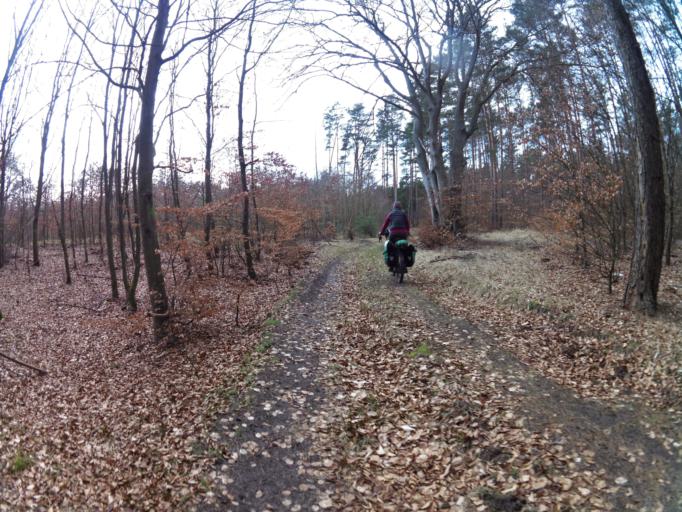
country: PL
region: Lubusz
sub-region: Powiat gorzowski
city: Witnica
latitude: 52.7661
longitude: 14.8350
